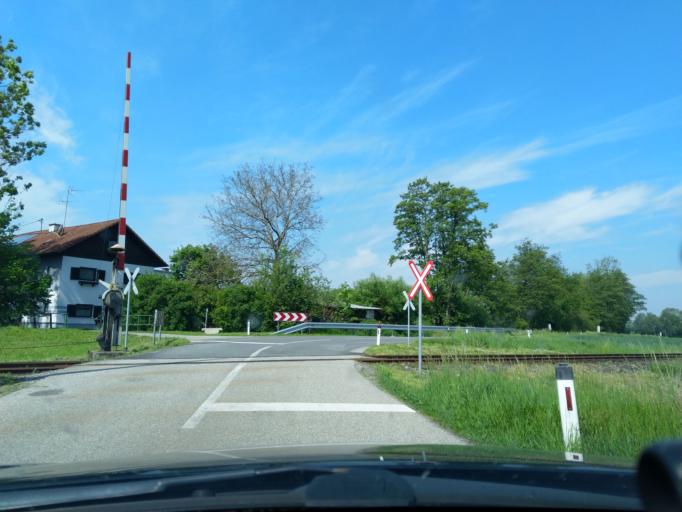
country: AT
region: Upper Austria
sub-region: Politischer Bezirk Scharding
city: Sankt Marienkirchen bei Schaerding
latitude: 48.2944
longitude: 13.4302
